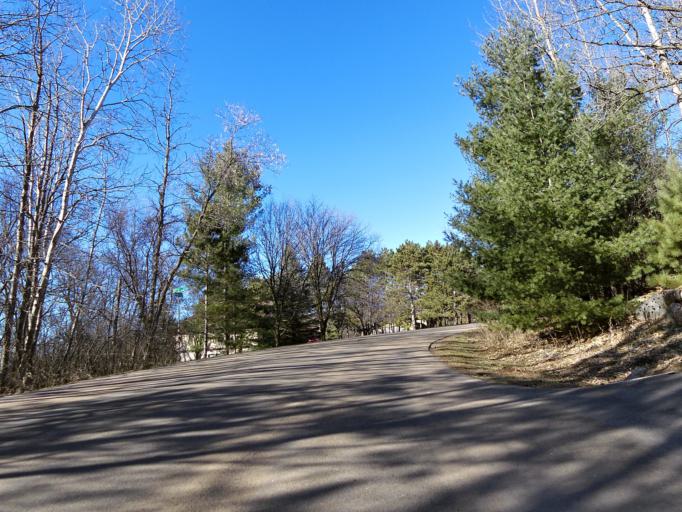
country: US
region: Minnesota
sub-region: Washington County
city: Lake Elmo
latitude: 44.9816
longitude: -92.8263
